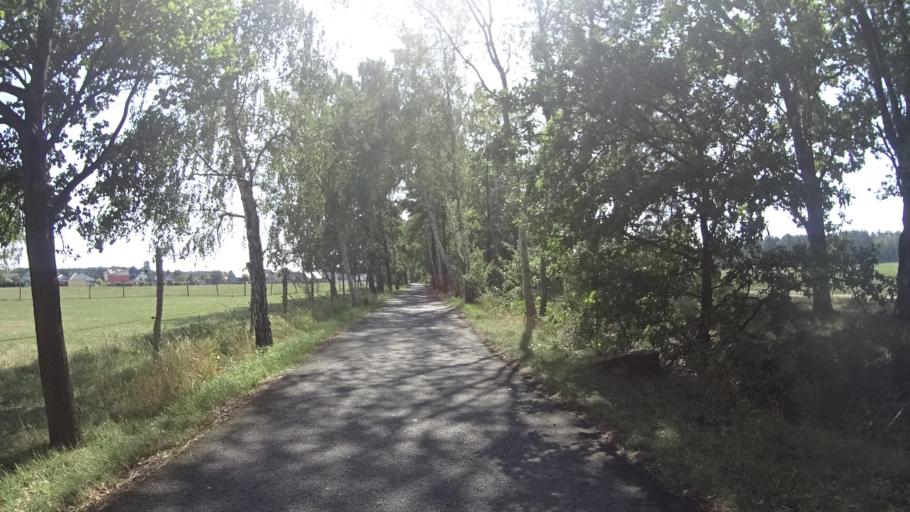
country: DE
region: Brandenburg
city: Cottbus
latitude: 51.7953
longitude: 14.2985
